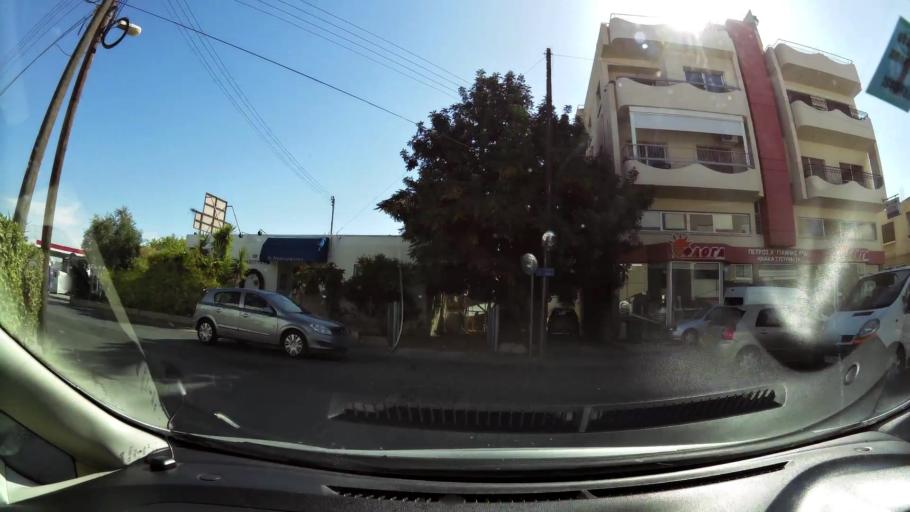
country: CY
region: Lefkosia
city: Nicosia
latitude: 35.1360
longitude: 33.3405
